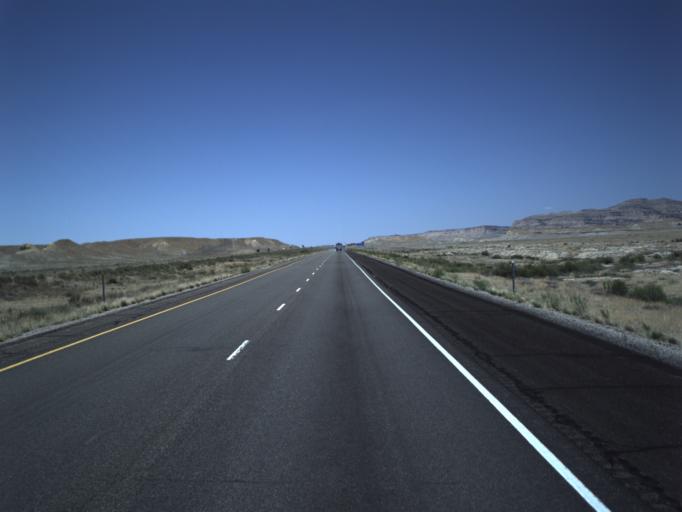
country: US
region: Utah
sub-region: Grand County
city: Moab
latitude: 38.9462
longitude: -109.6535
